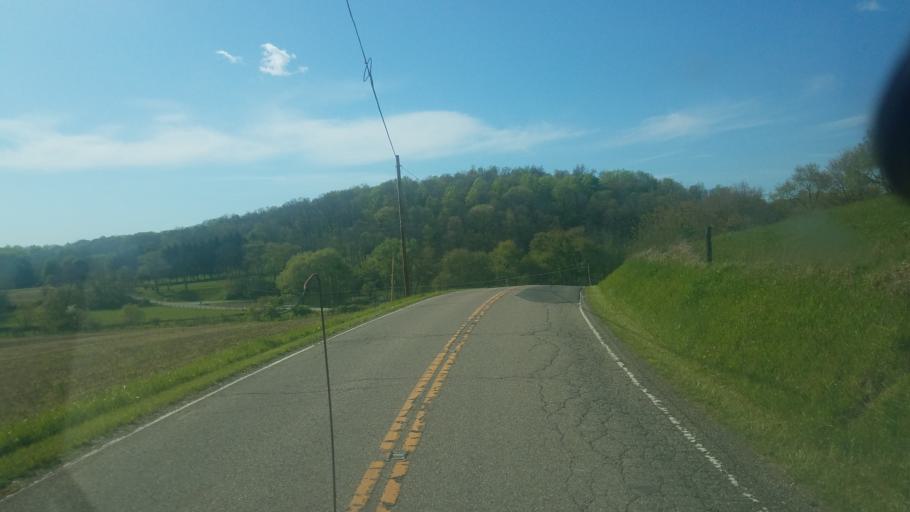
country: US
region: Ohio
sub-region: Coshocton County
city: Coshocton
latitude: 40.3389
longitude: -81.9253
